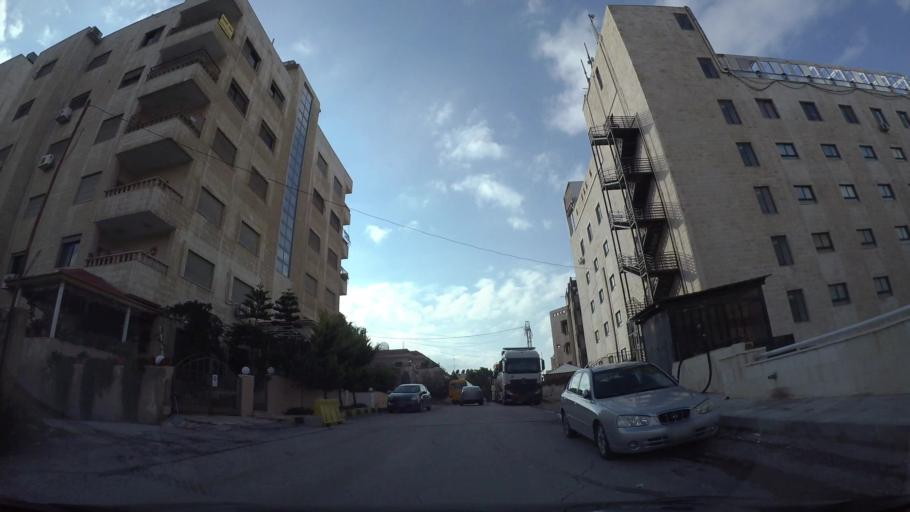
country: JO
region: Amman
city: Al Jubayhah
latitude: 31.9853
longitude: 35.8775
